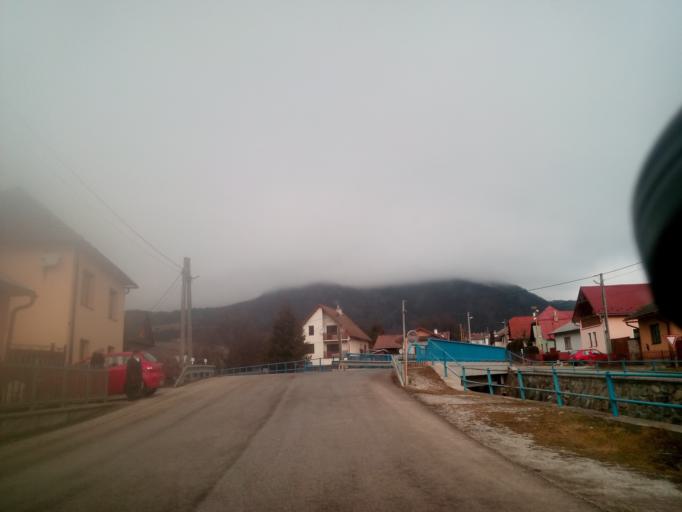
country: SK
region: Kosicky
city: Krompachy
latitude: 48.9310
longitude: 20.9399
